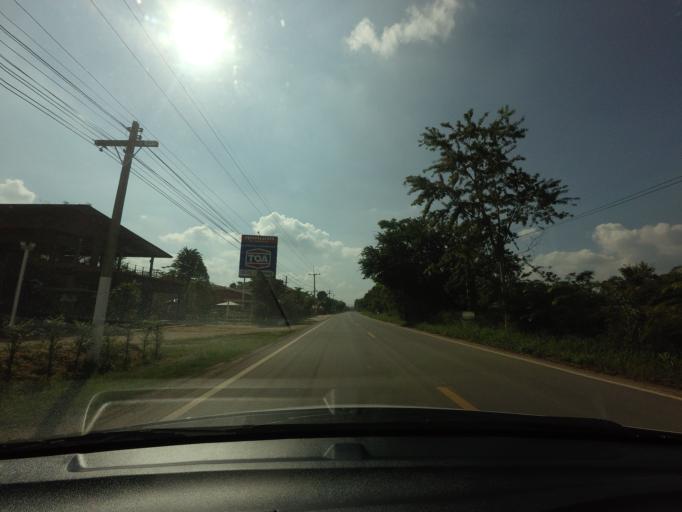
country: TH
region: Nakhon Ratchasima
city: Wang Nam Khiao
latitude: 14.4636
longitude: 101.6510
